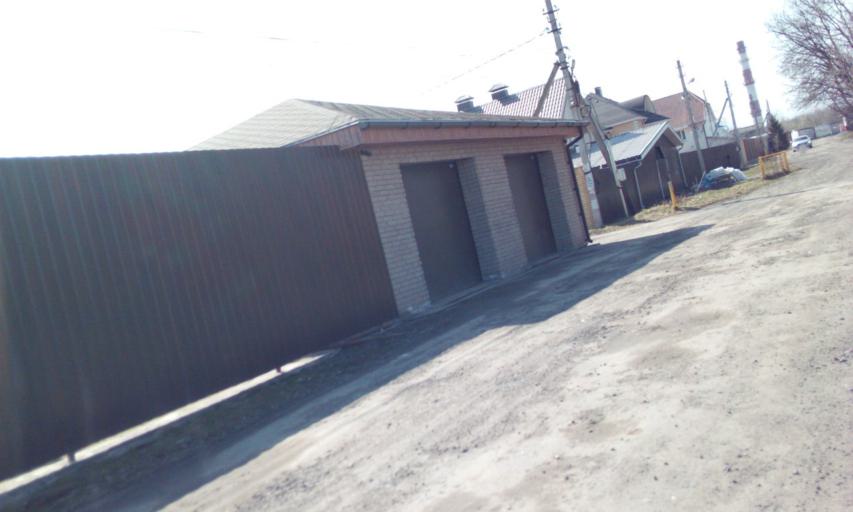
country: RU
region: Moskovskaya
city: Kommunarka
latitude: 55.5221
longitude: 37.4600
